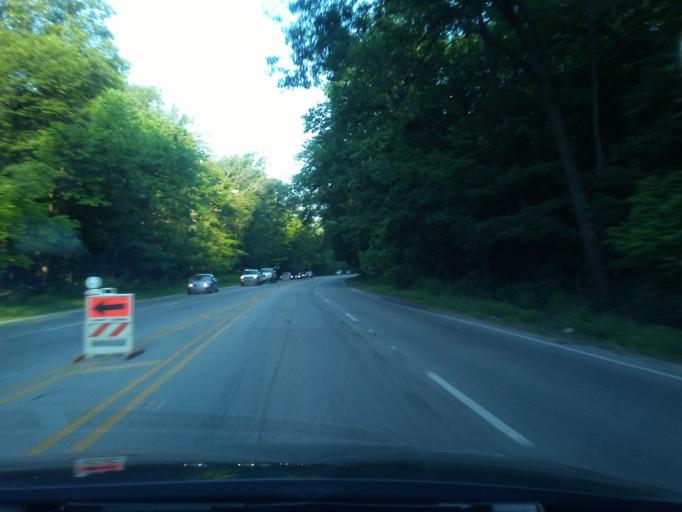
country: US
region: Illinois
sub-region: Cook County
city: Lincolnwood
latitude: 41.9972
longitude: -87.7693
